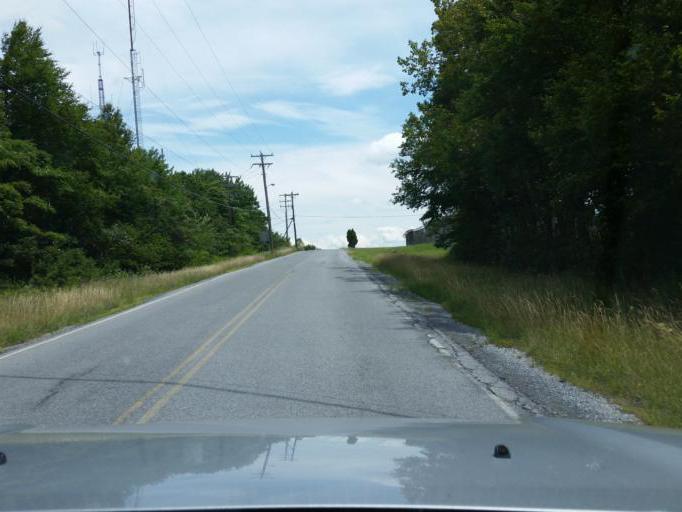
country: US
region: Pennsylvania
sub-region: Blair County
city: Altoona
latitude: 40.5674
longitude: -78.4423
